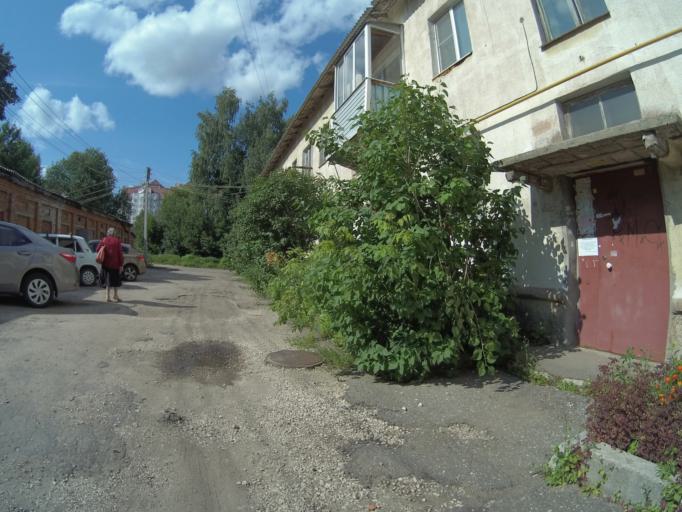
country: RU
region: Vladimir
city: Vladimir
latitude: 56.1424
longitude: 40.3955
